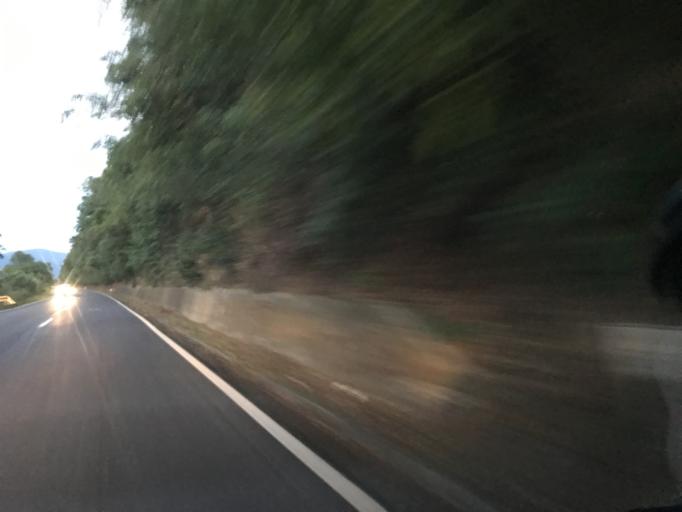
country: RO
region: Caras-Severin
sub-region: Comuna Berzasca
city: Liubcova
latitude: 44.6463
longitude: 21.8611
